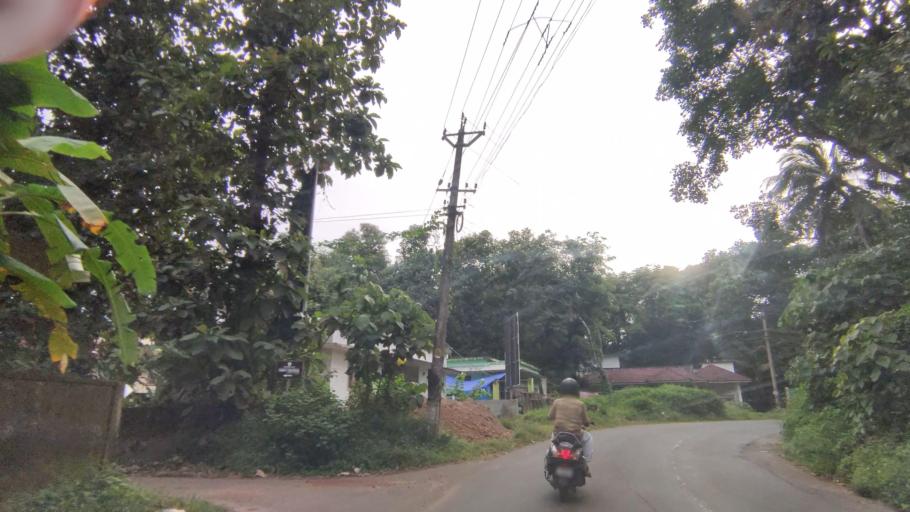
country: IN
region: Kerala
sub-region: Kottayam
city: Vaikam
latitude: 9.6921
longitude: 76.4734
